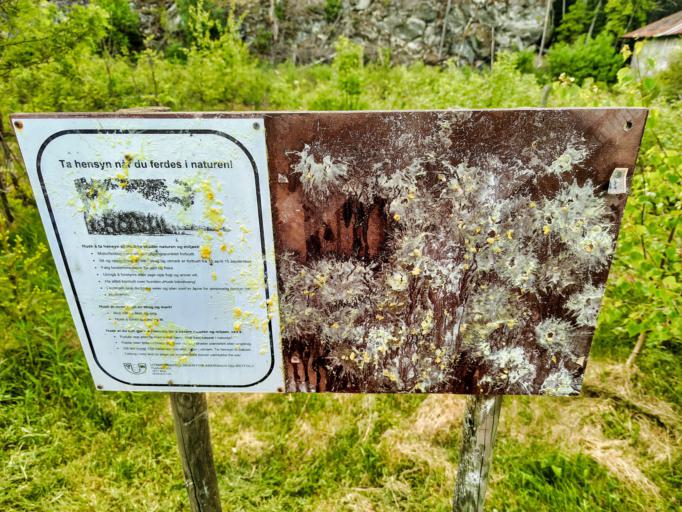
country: NO
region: Akershus
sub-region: Sorum
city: Sorumsand
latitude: 59.9552
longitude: 11.2151
